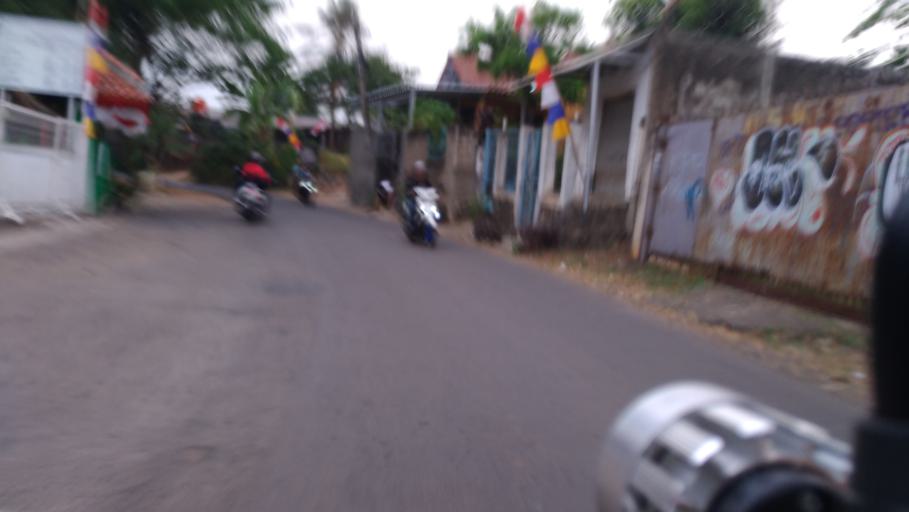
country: ID
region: West Java
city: Depok
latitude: -6.3452
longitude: 106.8689
